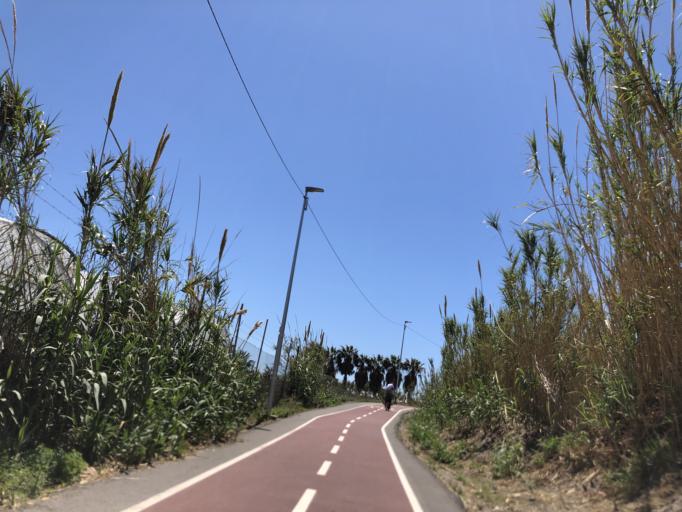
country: ES
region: Andalusia
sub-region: Provincia de Almeria
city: Almeria
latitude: 36.8354
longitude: -2.4038
